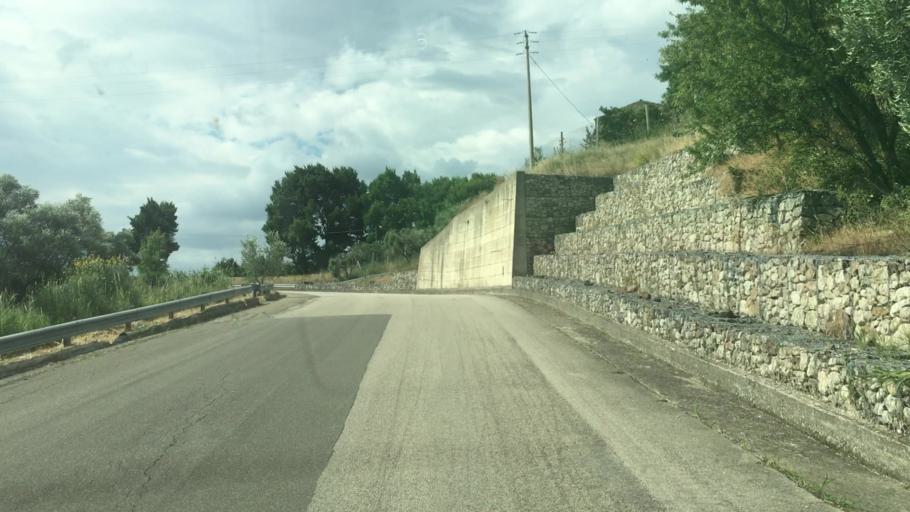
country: IT
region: Basilicate
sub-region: Provincia di Matera
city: San Mauro Forte
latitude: 40.4802
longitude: 16.2667
